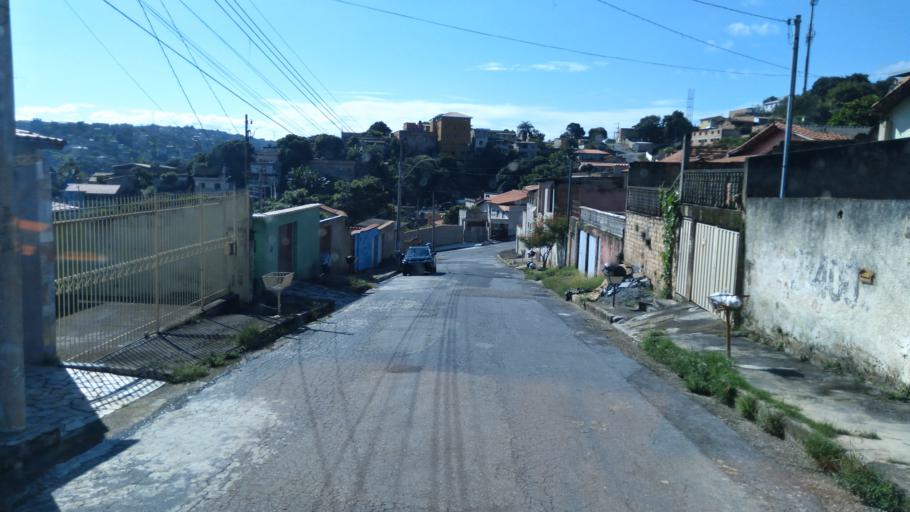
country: BR
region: Minas Gerais
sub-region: Santa Luzia
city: Santa Luzia
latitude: -19.8275
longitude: -43.9001
